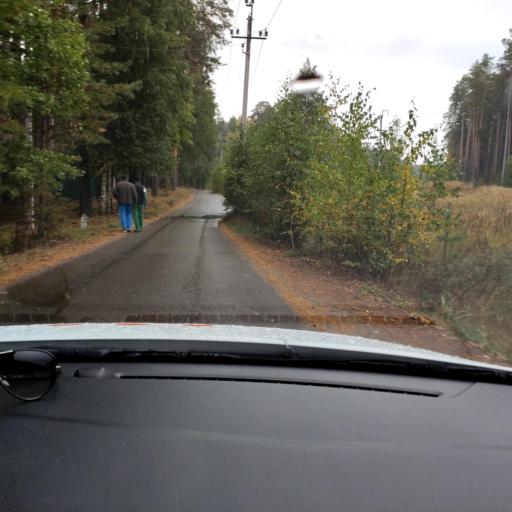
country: RU
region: Tatarstan
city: Verkhniy Uslon
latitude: 55.6413
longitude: 49.0191
